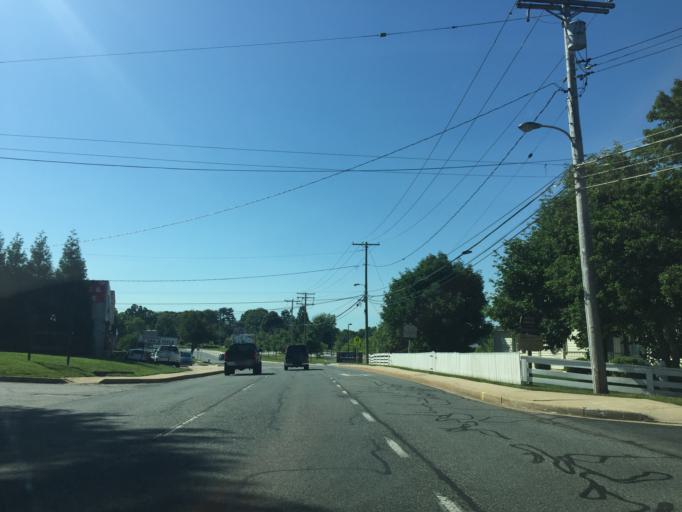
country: US
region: Maryland
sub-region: Harford County
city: Bel Air
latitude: 39.5329
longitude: -76.3473
